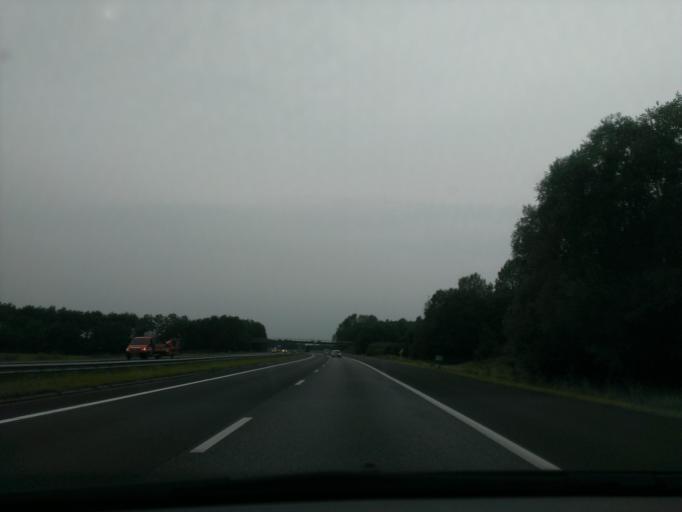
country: NL
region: Drenthe
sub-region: Gemeente Meppel
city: Meppel
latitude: 52.6860
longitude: 6.2407
